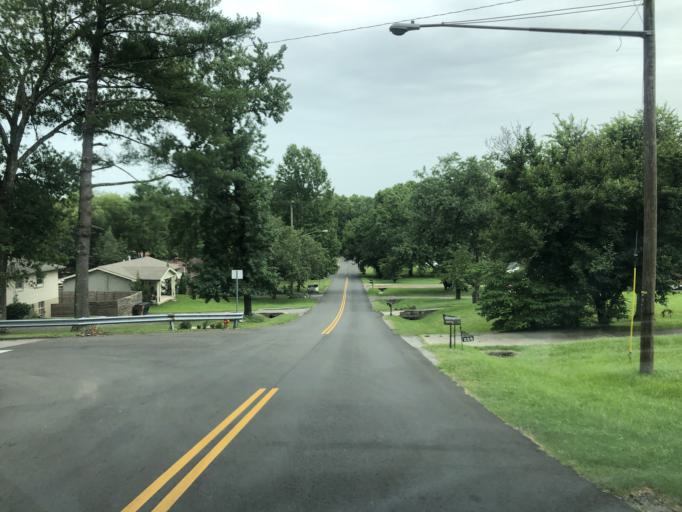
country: US
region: Tennessee
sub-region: Davidson County
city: Nashville
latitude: 36.1702
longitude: -86.7260
